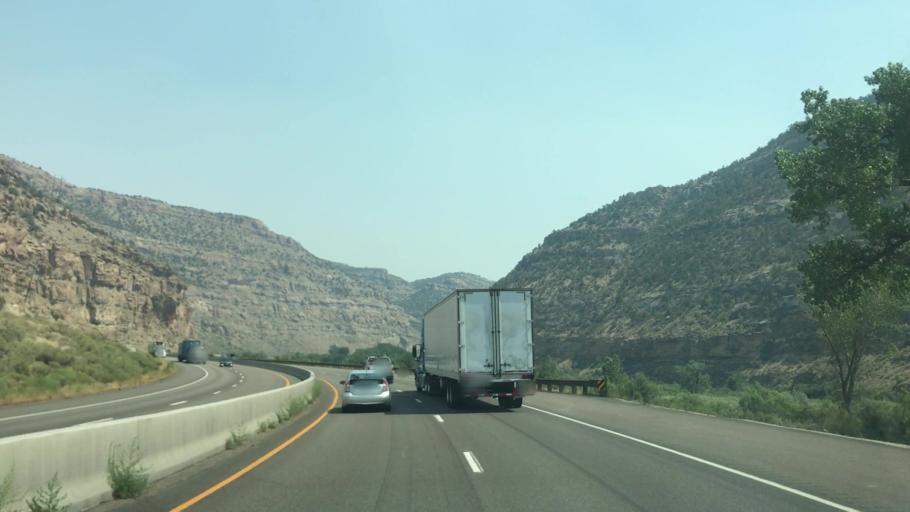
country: US
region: Colorado
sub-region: Mesa County
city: Palisade
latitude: 39.2309
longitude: -108.2708
